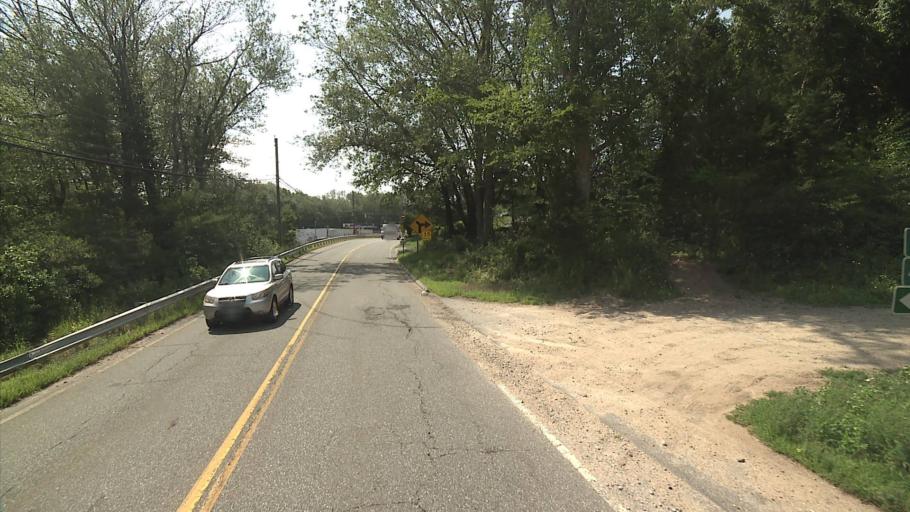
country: US
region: Connecticut
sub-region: New London County
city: Montville Center
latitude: 41.5027
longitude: -72.2000
